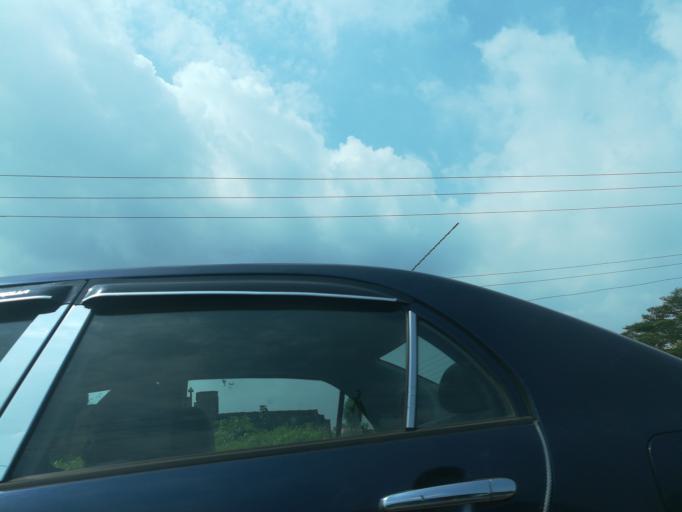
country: NG
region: Lagos
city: Ikorodu
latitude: 6.6006
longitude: 3.6249
